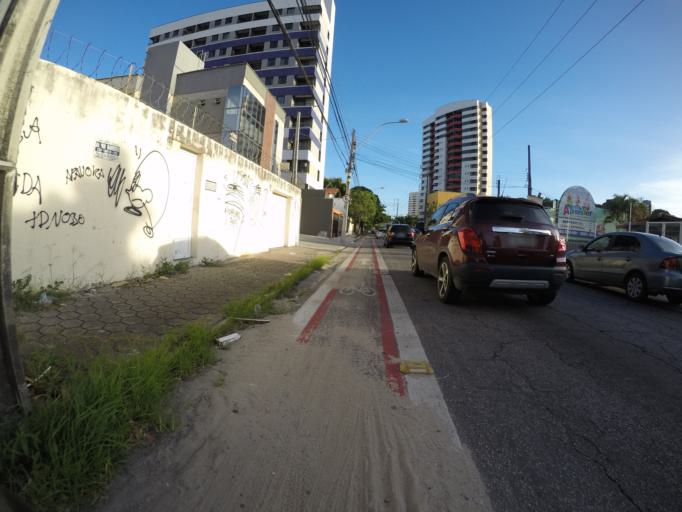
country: BR
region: Ceara
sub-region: Fortaleza
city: Fortaleza
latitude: -3.7454
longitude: -38.5124
